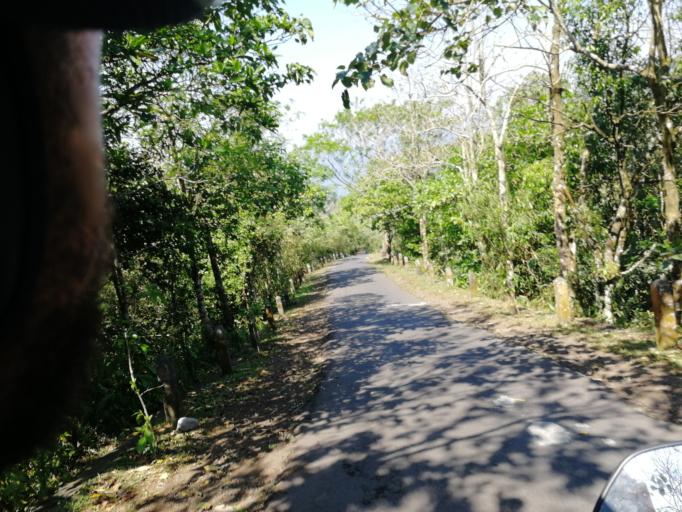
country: ID
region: Bali
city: Tiyingtali Kelod
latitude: -8.3908
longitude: 115.6394
